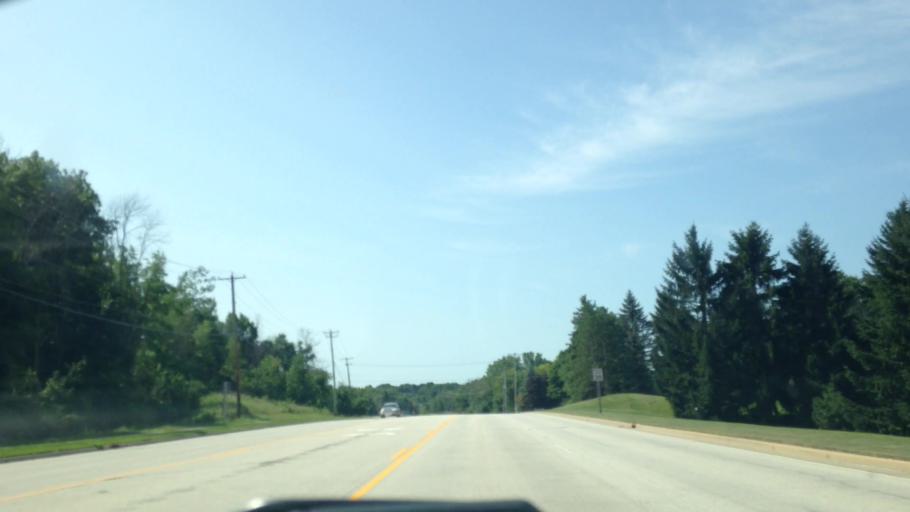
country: US
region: Wisconsin
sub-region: Waukesha County
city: Menomonee Falls
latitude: 43.1967
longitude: -88.1626
